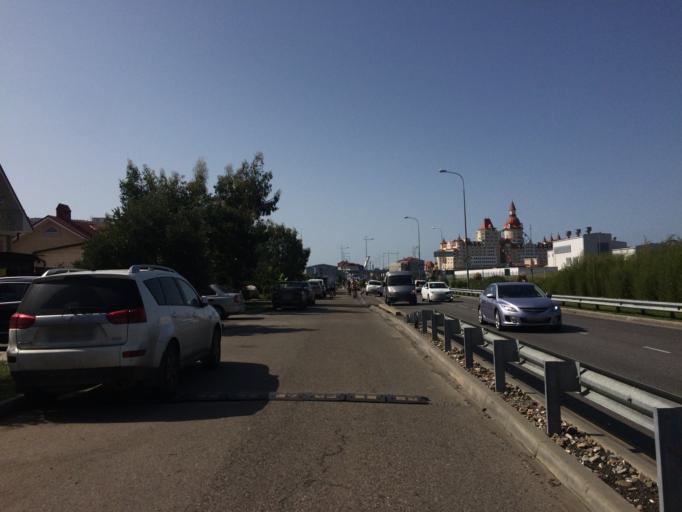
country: RU
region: Krasnodarskiy
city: Adler
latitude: 43.4003
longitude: 39.9695
